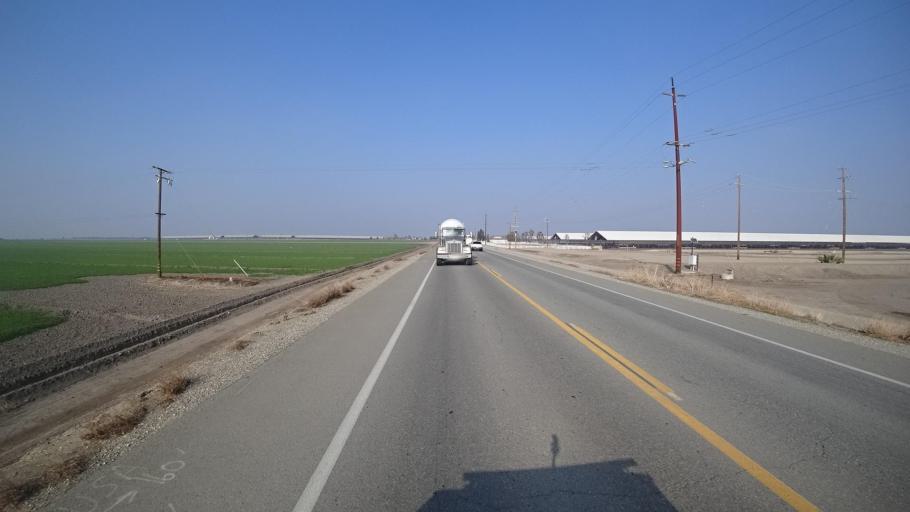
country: US
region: California
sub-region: Kern County
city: Greenfield
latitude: 35.1656
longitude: -119.1099
